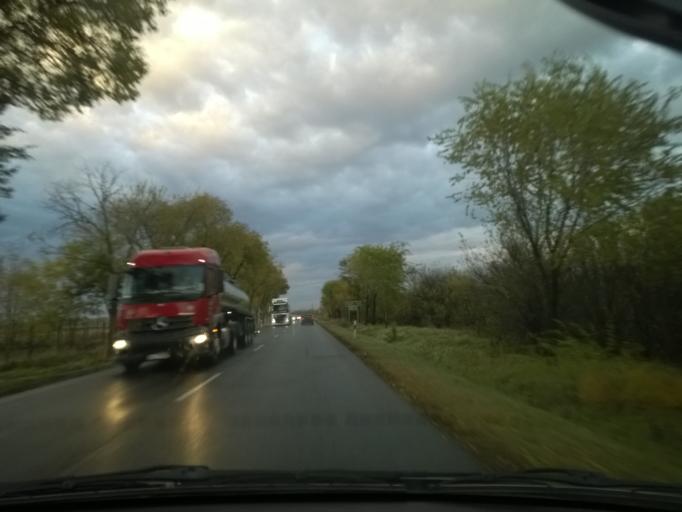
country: HU
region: Bacs-Kiskun
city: Solt
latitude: 46.8401
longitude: 19.0060
